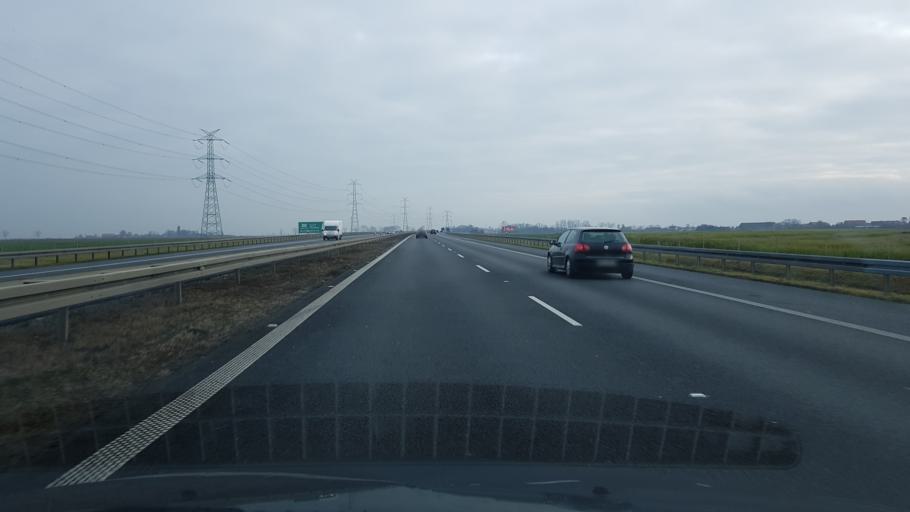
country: PL
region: Lower Silesian Voivodeship
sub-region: Powiat olawski
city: Wierzbno
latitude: 50.8987
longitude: 17.1746
